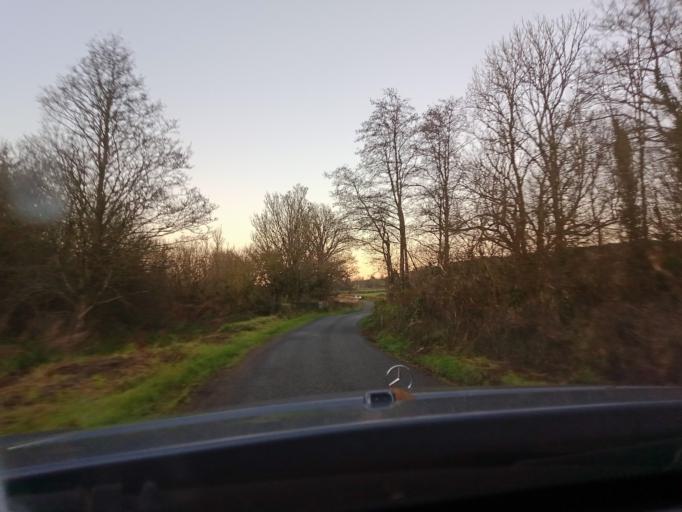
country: IE
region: Leinster
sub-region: Kilkenny
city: Thomastown
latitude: 52.4380
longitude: -7.1083
